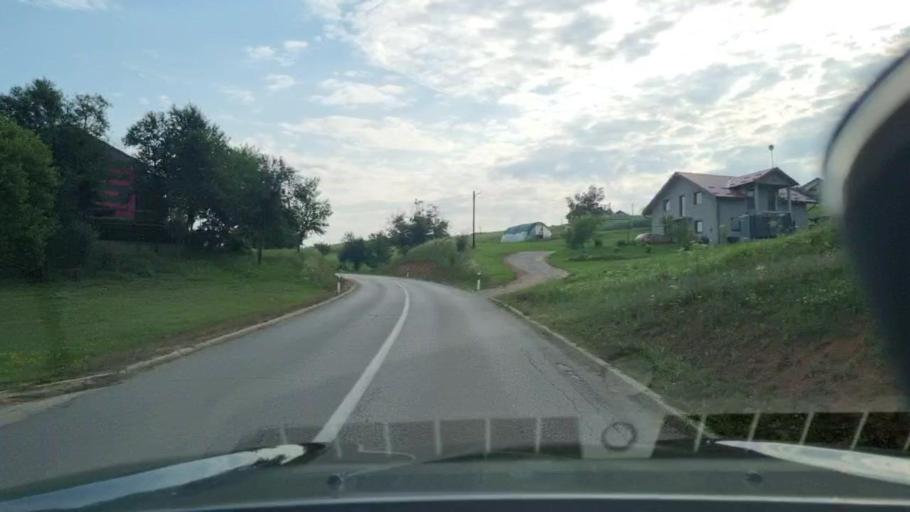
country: BA
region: Federation of Bosnia and Herzegovina
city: Podzvizd
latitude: 45.1756
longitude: 15.8558
